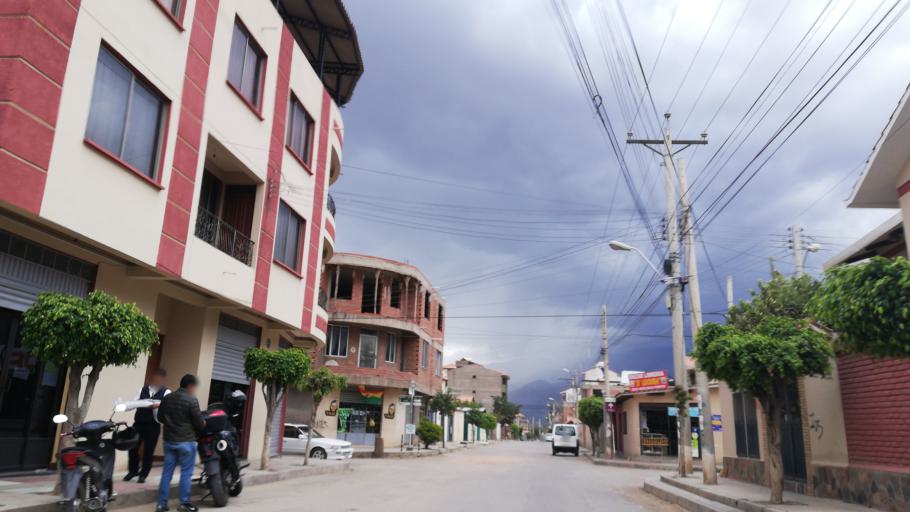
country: BO
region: Cochabamba
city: Cochabamba
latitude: -17.3405
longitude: -66.2191
